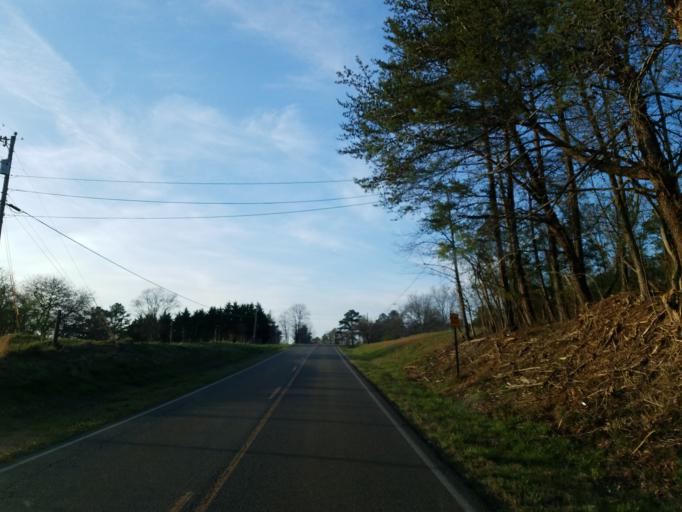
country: US
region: Georgia
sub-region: Pickens County
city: Jasper
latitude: 34.4933
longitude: -84.5160
